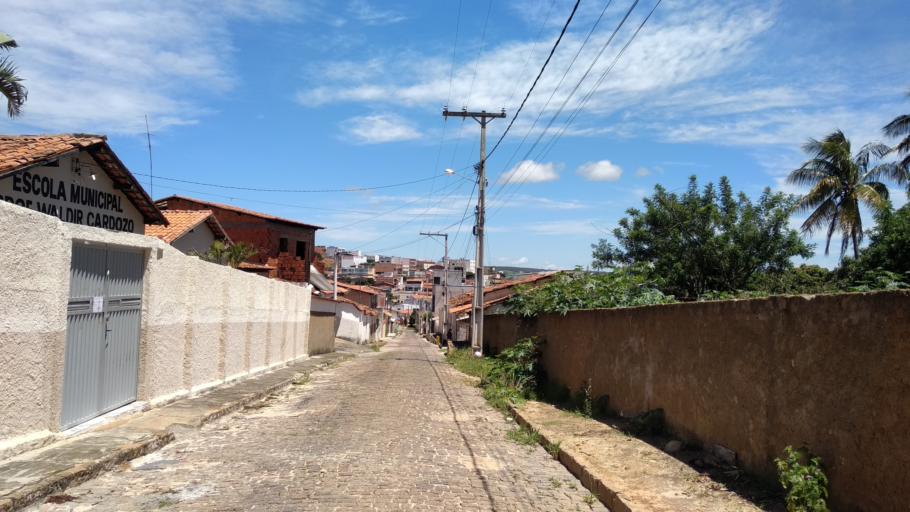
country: BR
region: Bahia
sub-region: Caetite
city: Caetite
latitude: -14.0698
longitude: -42.4815
